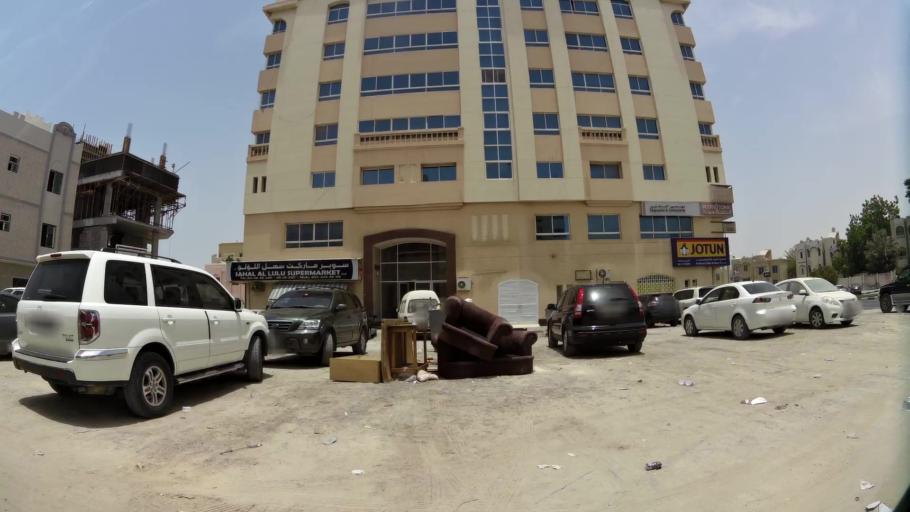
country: AE
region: Ash Shariqah
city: Sharjah
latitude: 25.3546
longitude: 55.3966
